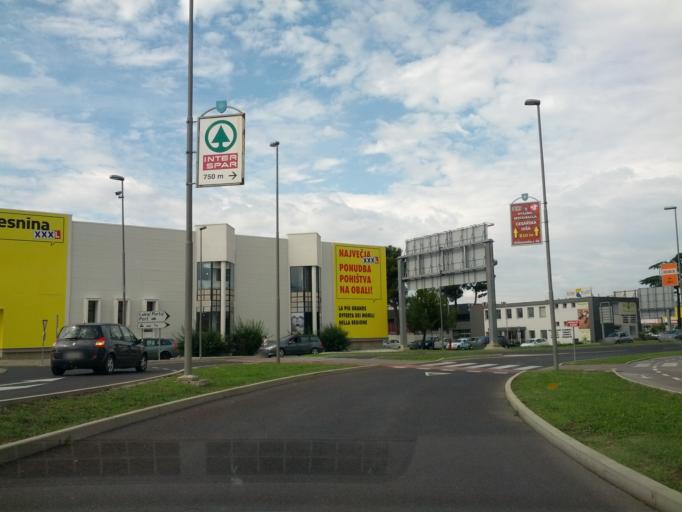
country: SI
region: Koper-Capodistria
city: Koper
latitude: 45.5404
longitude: 13.7332
